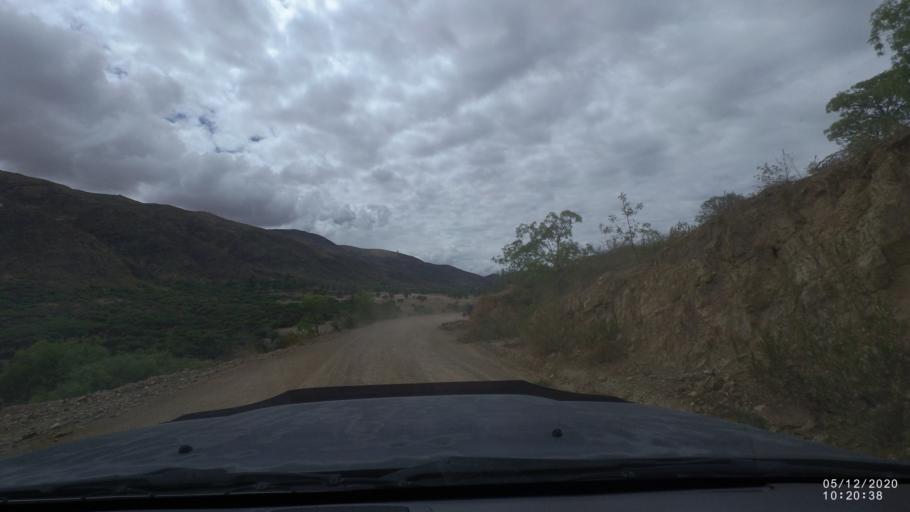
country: BO
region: Cochabamba
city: Sipe Sipe
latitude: -17.4849
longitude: -66.2829
